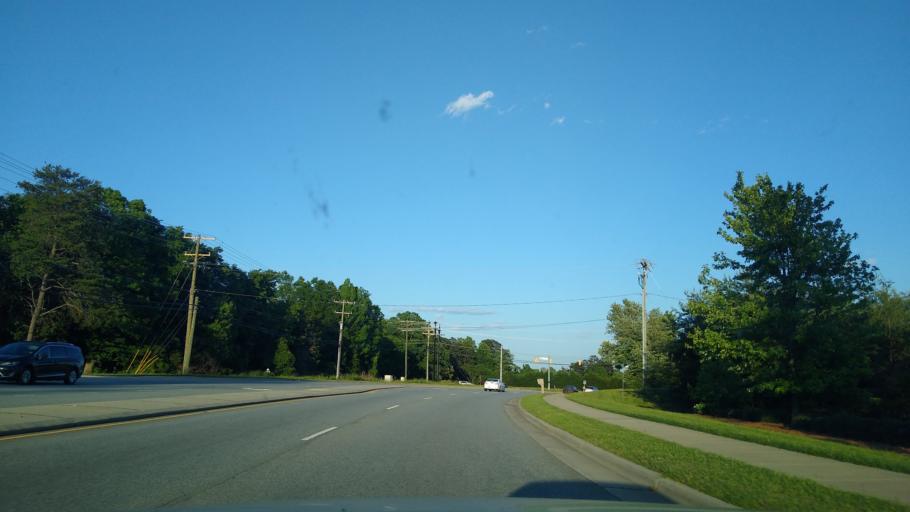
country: US
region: North Carolina
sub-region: Guilford County
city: Oak Ridge
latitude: 36.1044
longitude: -79.9858
